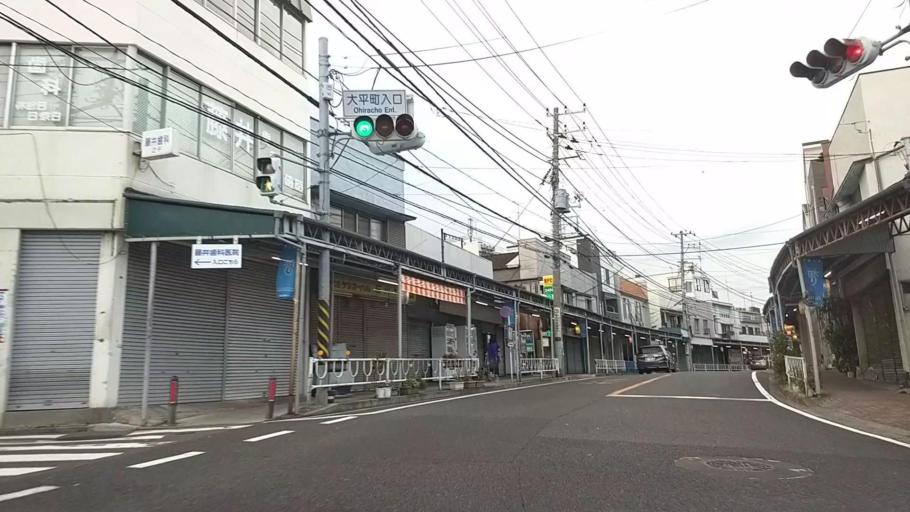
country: JP
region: Kanagawa
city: Yokohama
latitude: 35.4298
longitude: 139.6375
